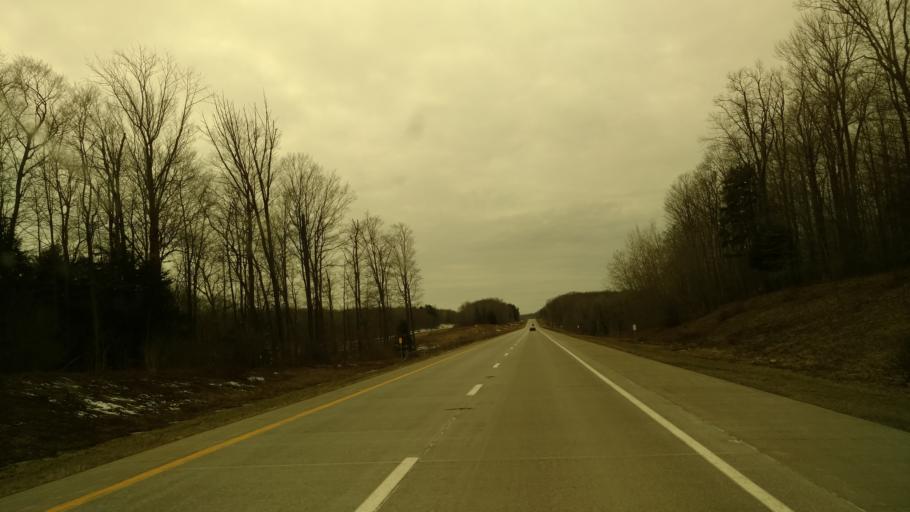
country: US
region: New York
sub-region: Chautauqua County
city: Mayville
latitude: 42.1543
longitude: -79.4475
